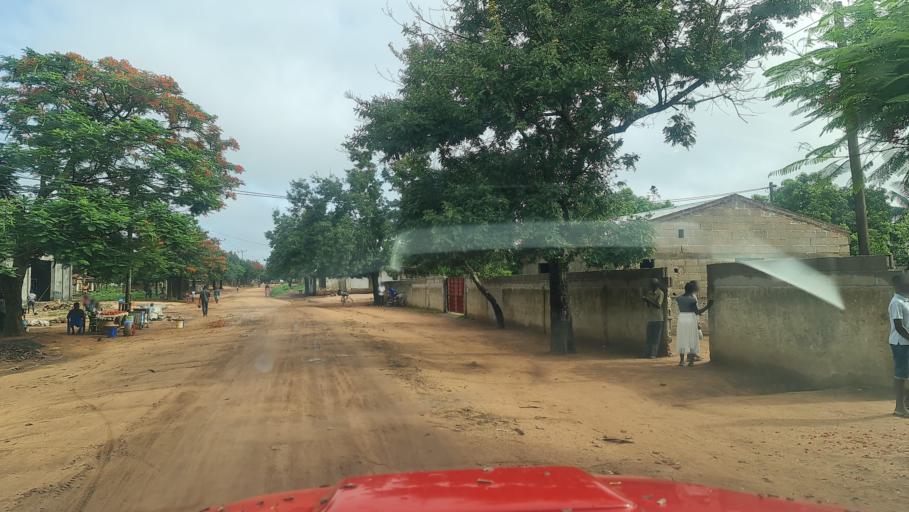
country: MW
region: Southern Region
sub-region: Nsanje District
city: Nsanje
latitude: -17.3250
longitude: 35.5916
